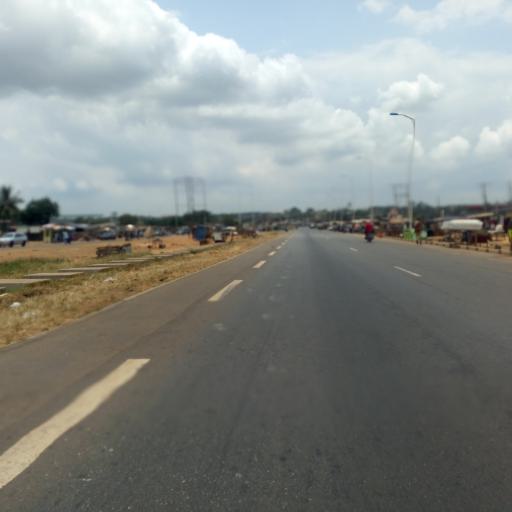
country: TG
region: Maritime
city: Tsevie
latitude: 6.3225
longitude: 1.2182
